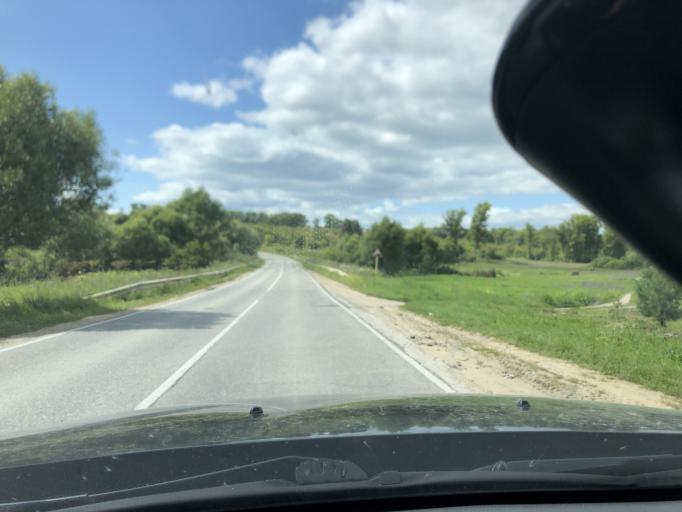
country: RU
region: Tula
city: Revyakino
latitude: 54.3455
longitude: 37.6128
